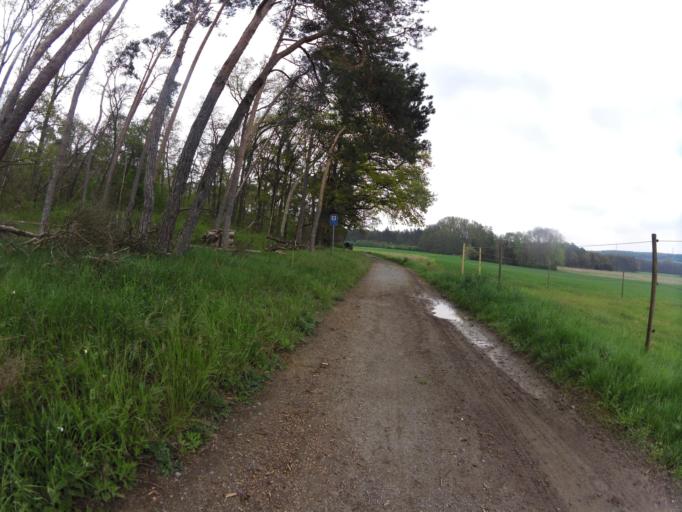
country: DE
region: Bavaria
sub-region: Regierungsbezirk Unterfranken
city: Sommerhausen
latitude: 49.7003
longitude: 10.0484
